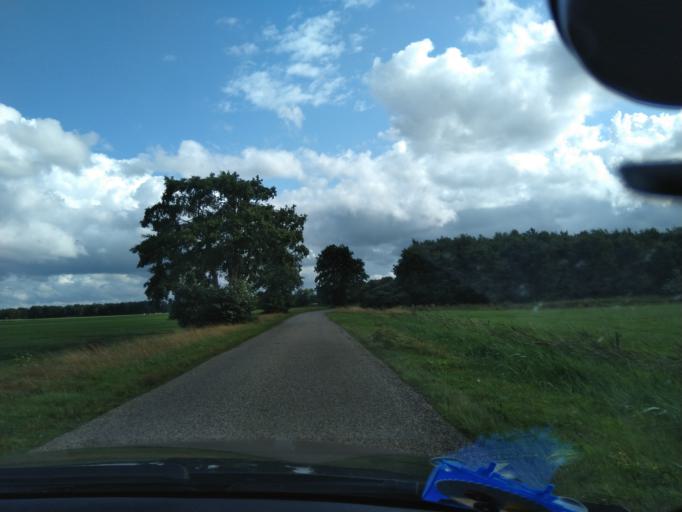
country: NL
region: Drenthe
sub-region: Gemeente Tynaarlo
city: Vries
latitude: 53.0649
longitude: 6.5462
